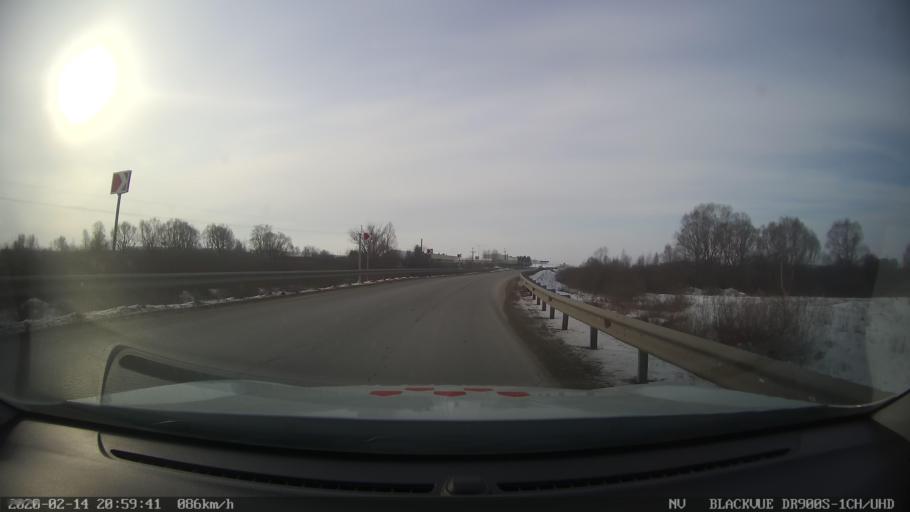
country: RU
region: Tatarstan
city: Kuybyshevskiy Zaton
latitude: 55.1765
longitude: 49.2350
